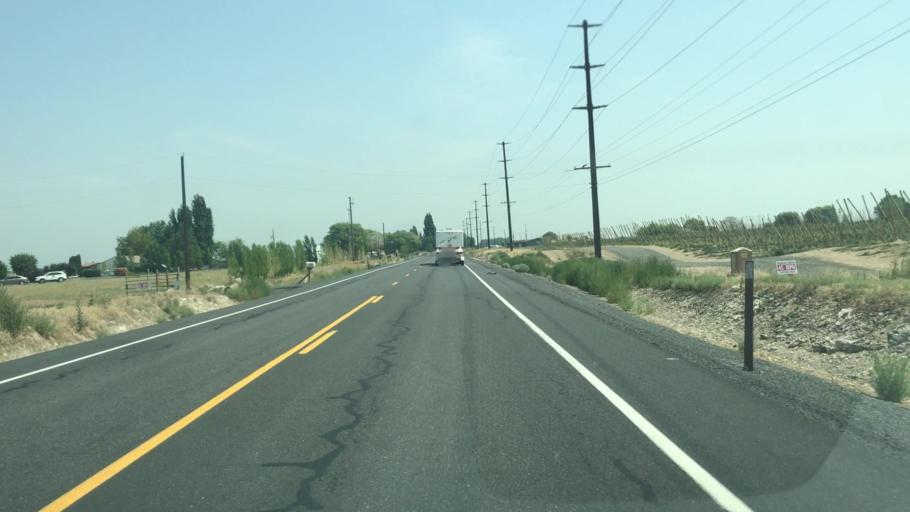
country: US
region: Washington
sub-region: Grant County
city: Quincy
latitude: 47.1604
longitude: -119.8833
